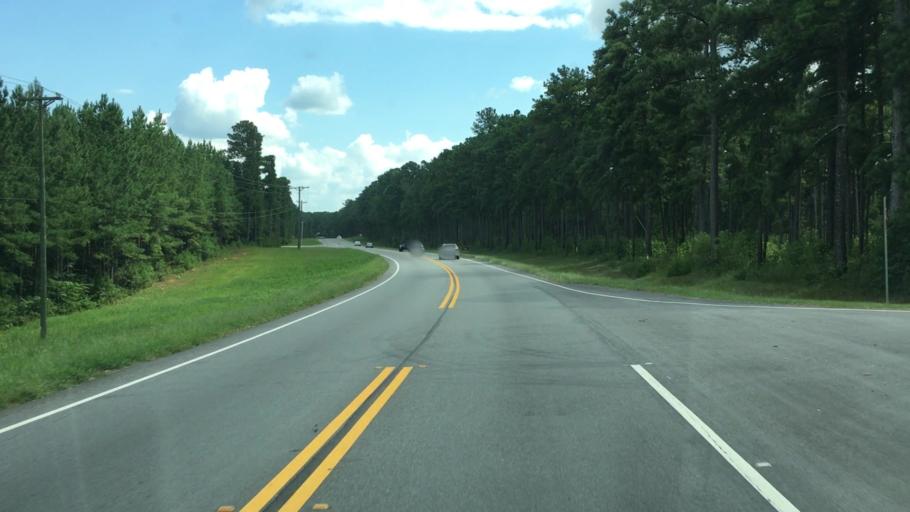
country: US
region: Georgia
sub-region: Putnam County
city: Jefferson
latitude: 33.4131
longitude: -83.3720
